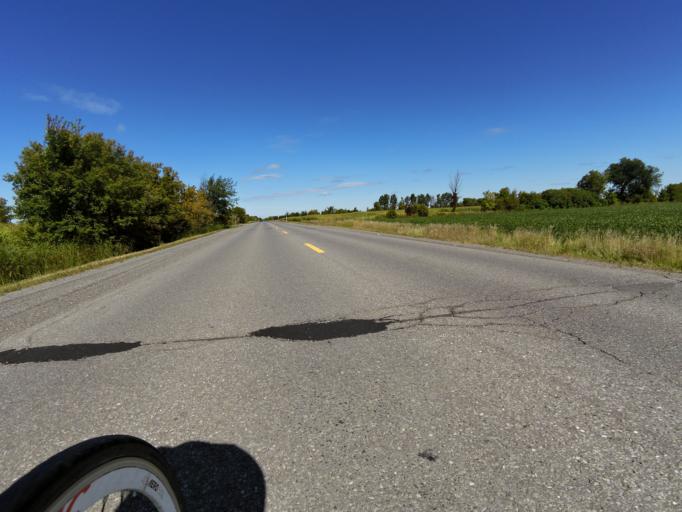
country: CA
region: Ontario
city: Bells Corners
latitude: 45.2271
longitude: -75.8351
